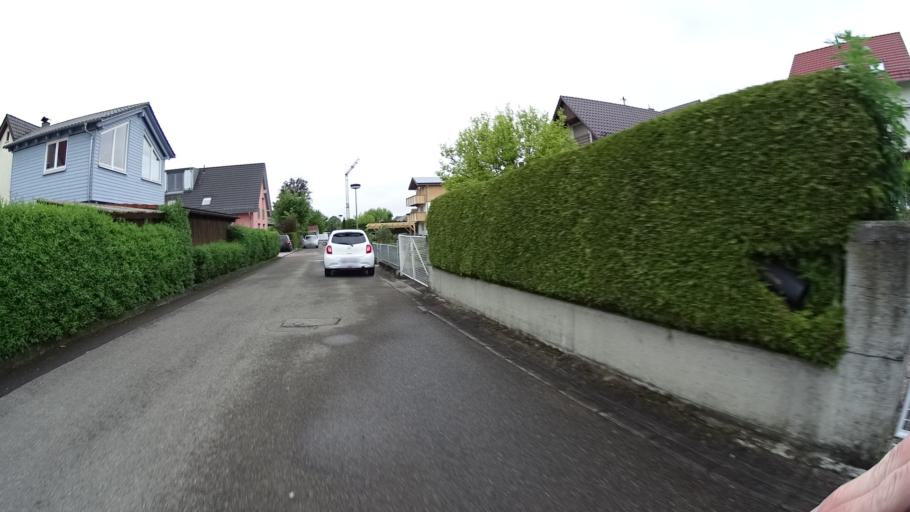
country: DE
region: Bavaria
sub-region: Swabia
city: Pfaffenhofen an der Roth
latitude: 48.3566
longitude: 10.1636
